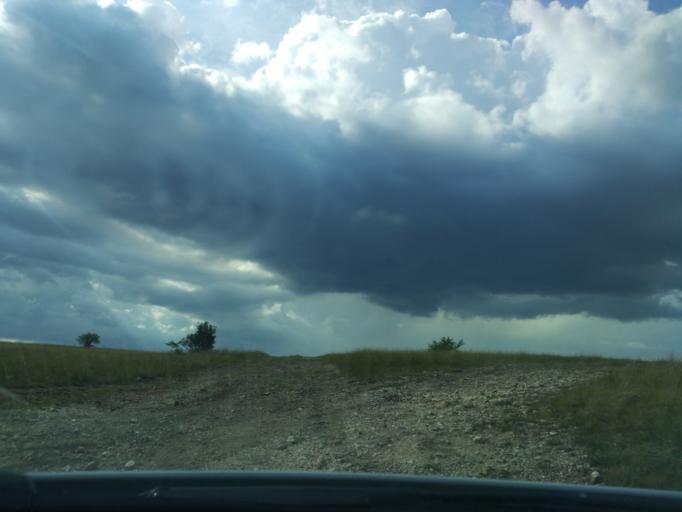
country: HU
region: Veszprem
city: Varpalota
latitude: 47.2243
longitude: 18.1430
